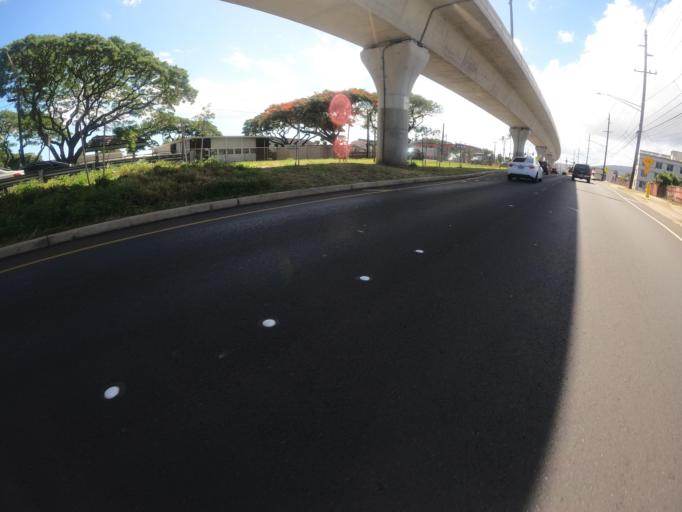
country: US
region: Hawaii
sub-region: Honolulu County
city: Waipahu
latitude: 21.3829
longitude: -158.0121
